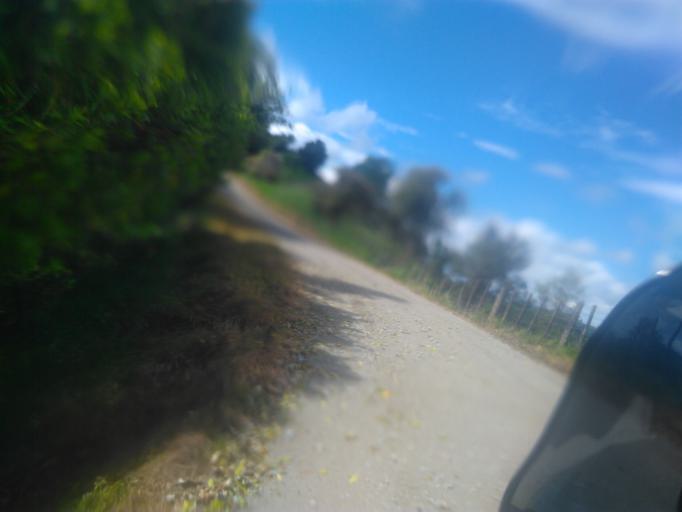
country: NZ
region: Hawke's Bay
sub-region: Wairoa District
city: Wairoa
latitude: -38.7722
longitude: 177.6382
